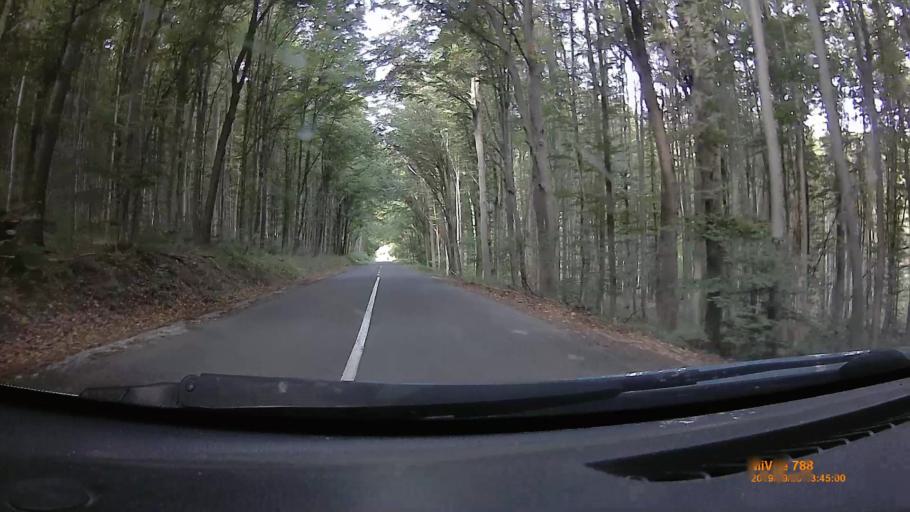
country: HU
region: Borsod-Abauj-Zemplen
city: Saly
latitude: 48.0621
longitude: 20.5641
